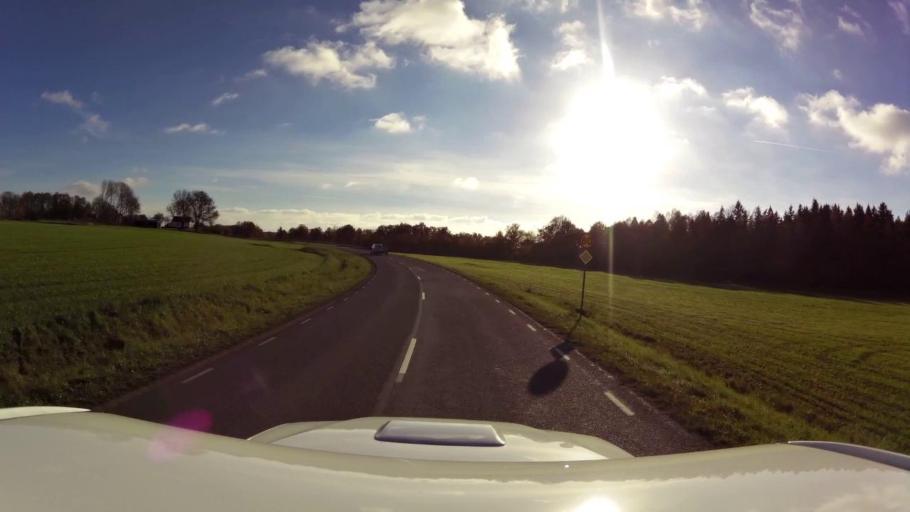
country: SE
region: OEstergoetland
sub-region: Linkopings Kommun
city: Malmslatt
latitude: 58.3363
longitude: 15.5127
